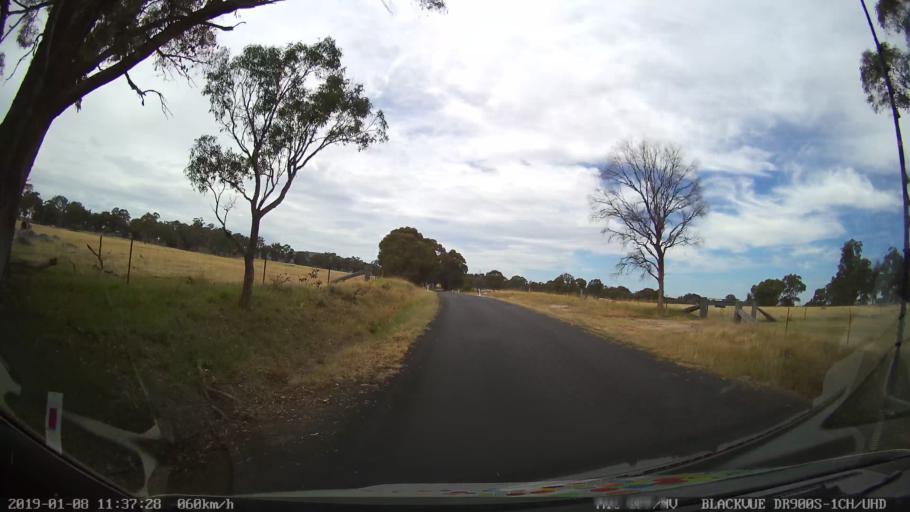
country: AU
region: New South Wales
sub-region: Guyra
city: Guyra
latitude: -30.3524
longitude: 151.5517
